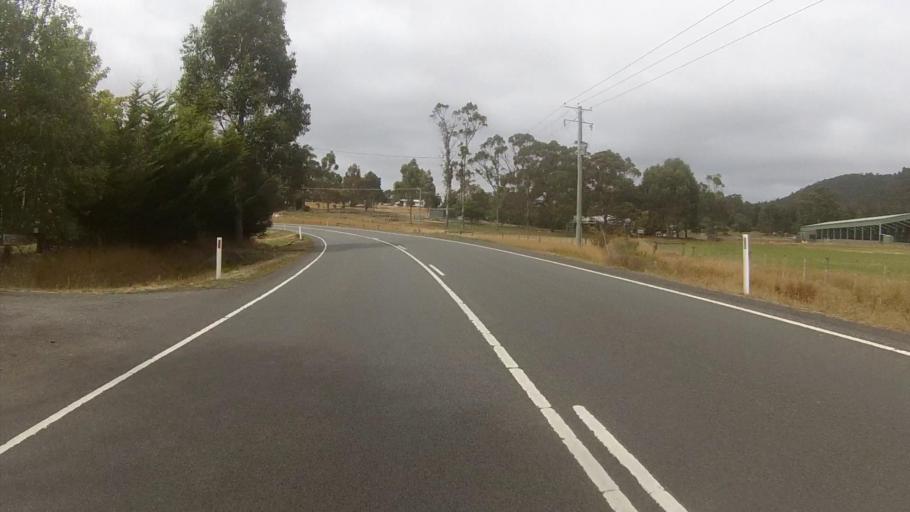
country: AU
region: Tasmania
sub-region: Kingborough
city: Margate
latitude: -42.9912
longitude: 147.1981
